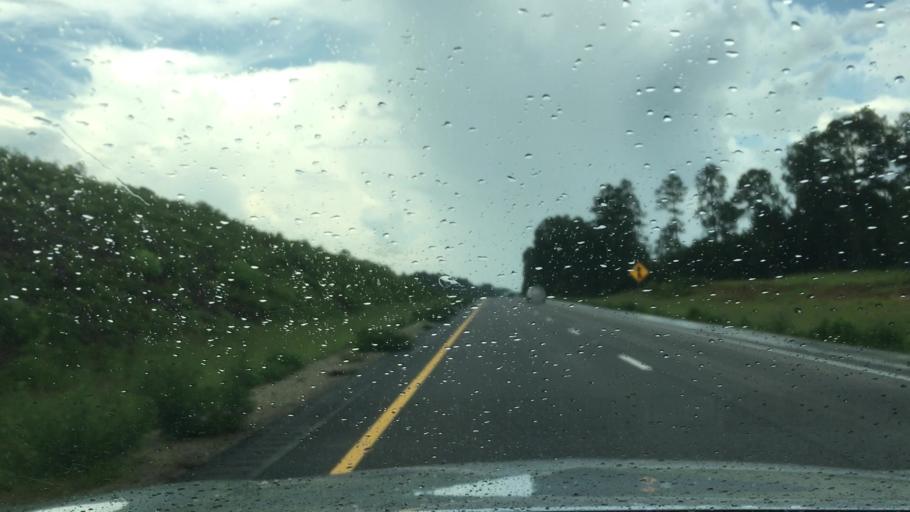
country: US
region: Mississippi
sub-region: Lamar County
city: Purvis
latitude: 31.2021
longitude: -89.3367
